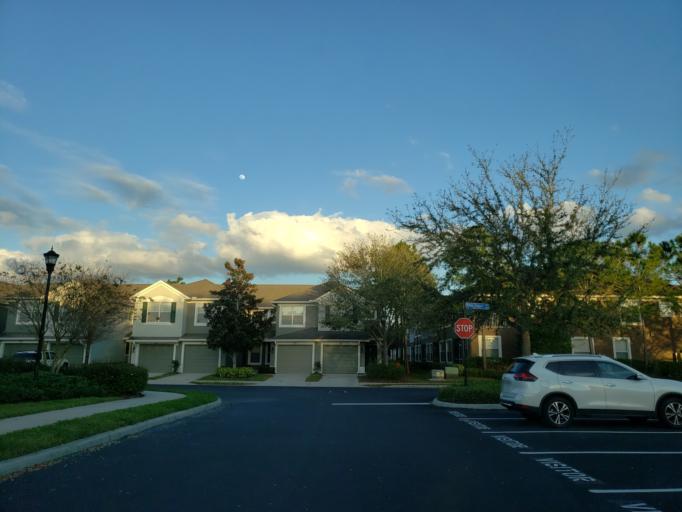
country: US
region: Florida
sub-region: Hillsborough County
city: Progress Village
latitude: 27.8989
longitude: -82.3339
